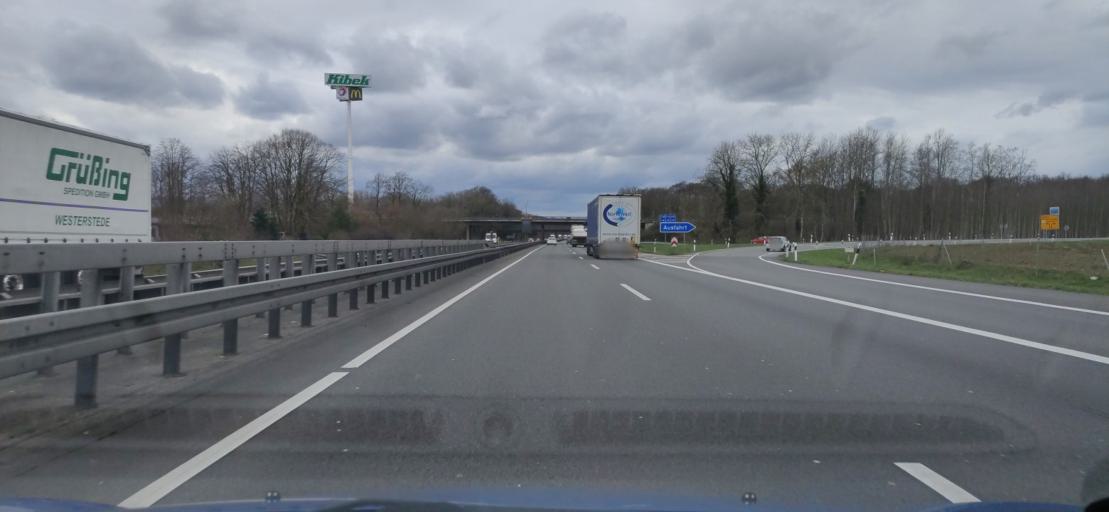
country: DE
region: Lower Saxony
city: Hasbergen
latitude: 52.2684
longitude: 7.9655
